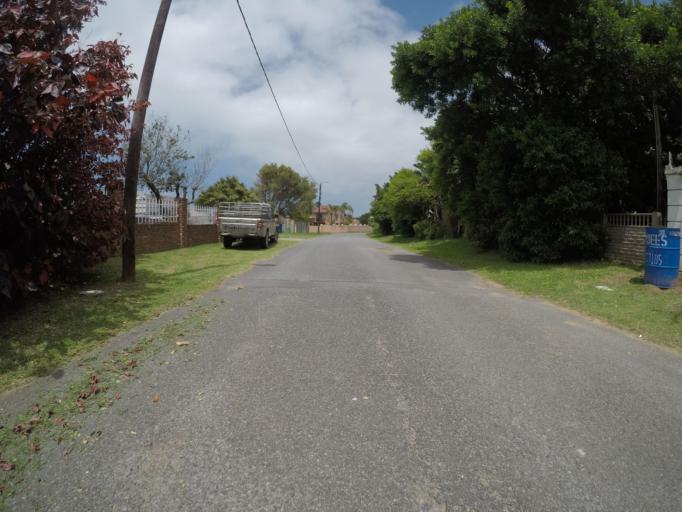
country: ZA
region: Eastern Cape
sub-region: Buffalo City Metropolitan Municipality
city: East London
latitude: -32.9400
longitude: 28.0166
